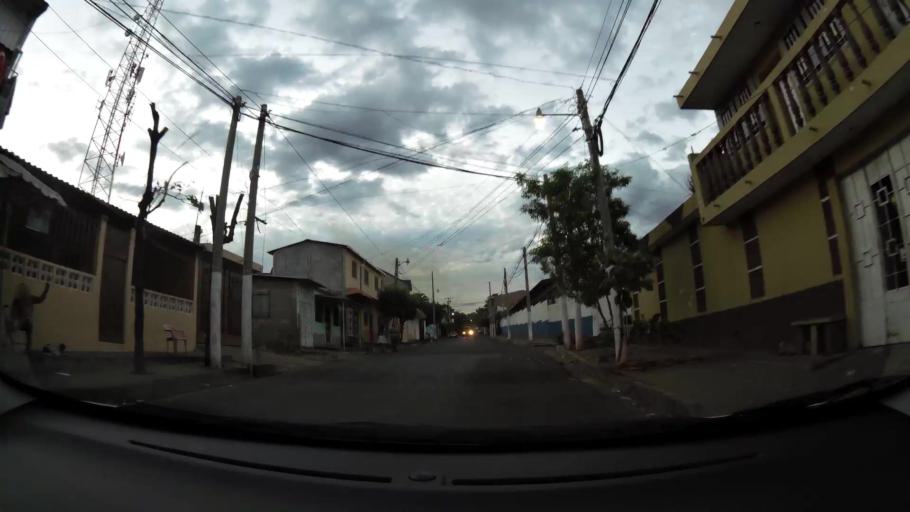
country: SV
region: San Vicente
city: San Vicente
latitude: 13.6415
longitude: -88.7895
